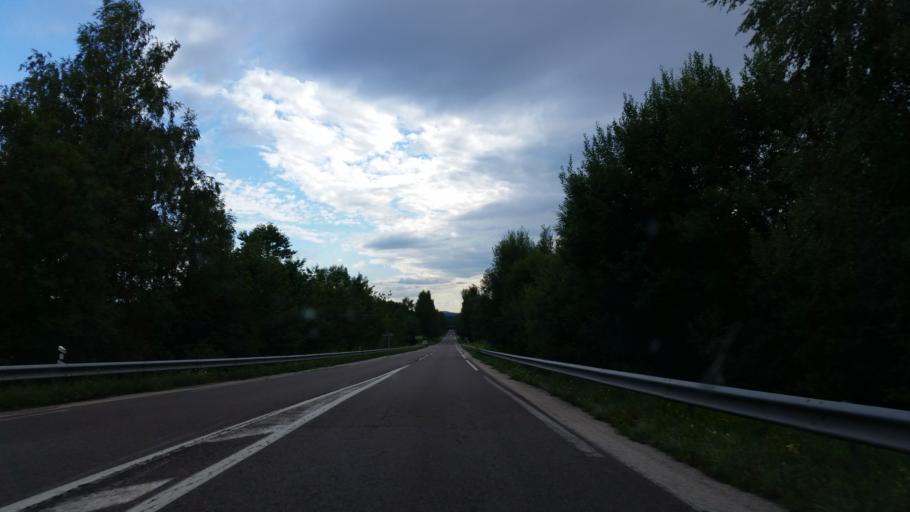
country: FR
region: Franche-Comte
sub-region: Departement de la Haute-Saone
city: Fougerolles
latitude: 47.9008
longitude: 6.4042
